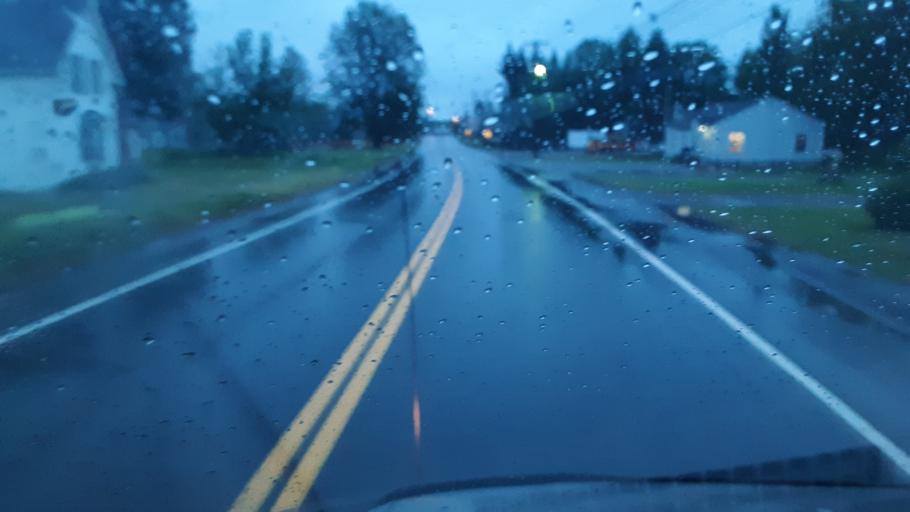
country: US
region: Maine
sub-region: Penobscot County
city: Patten
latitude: 45.9009
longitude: -68.4315
